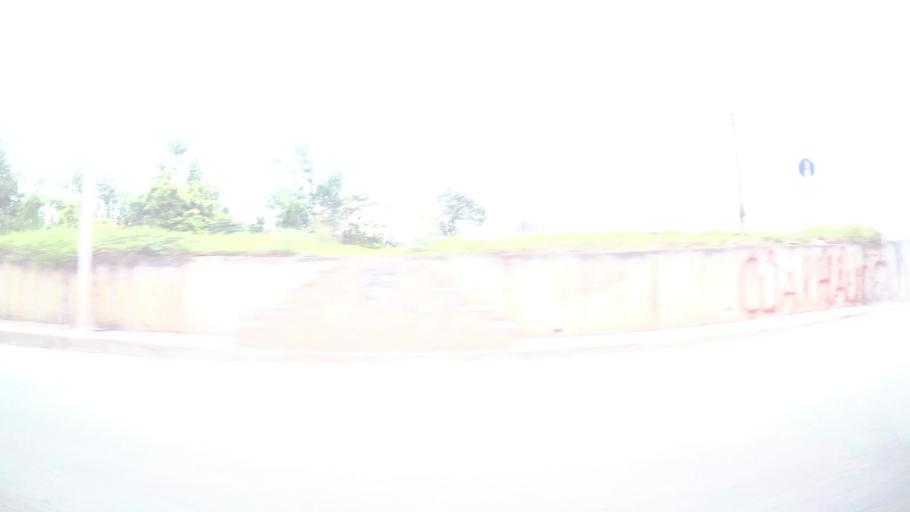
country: VN
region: Ha Noi
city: Trau Quy
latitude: 21.0610
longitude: 105.9203
